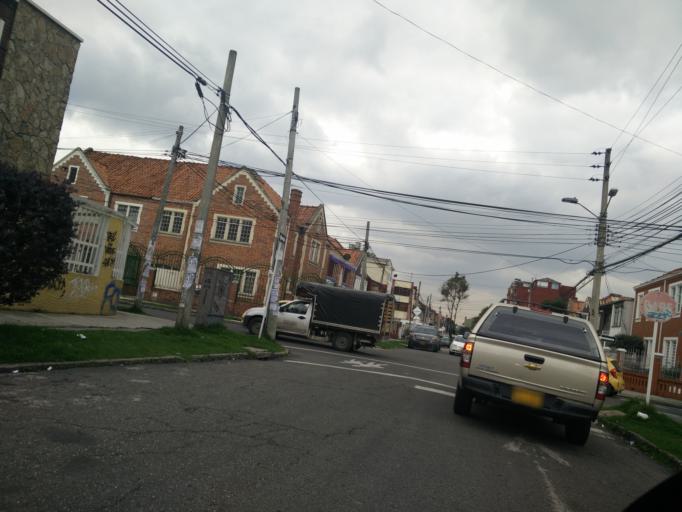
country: CO
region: Bogota D.C.
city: Bogota
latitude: 4.6516
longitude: -74.0691
